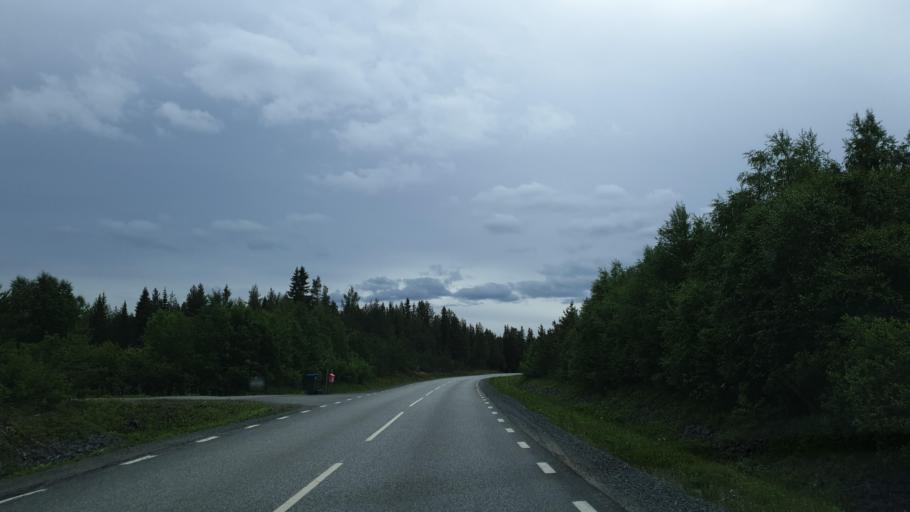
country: SE
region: Vaesterbotten
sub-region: Sorsele Kommun
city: Sorsele
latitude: 65.5251
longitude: 17.3901
